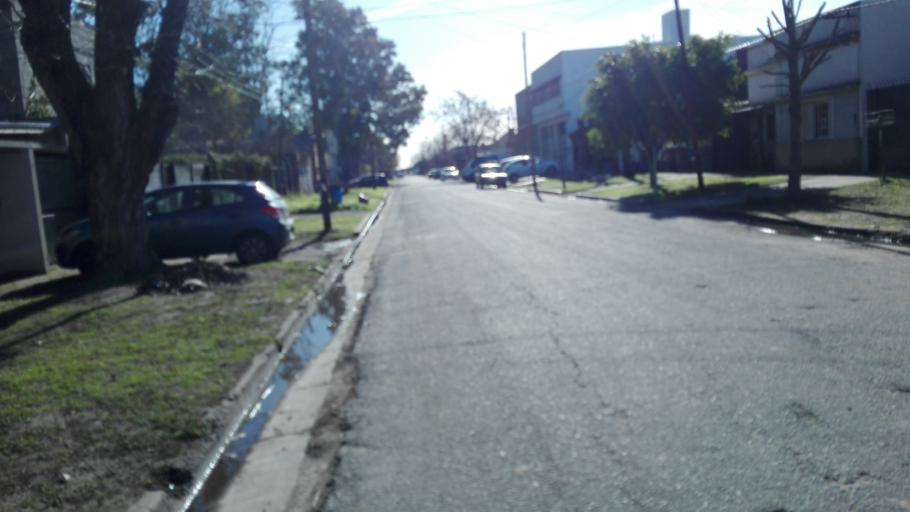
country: AR
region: Buenos Aires
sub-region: Partido de La Plata
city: La Plata
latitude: -34.8823
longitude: -57.9887
